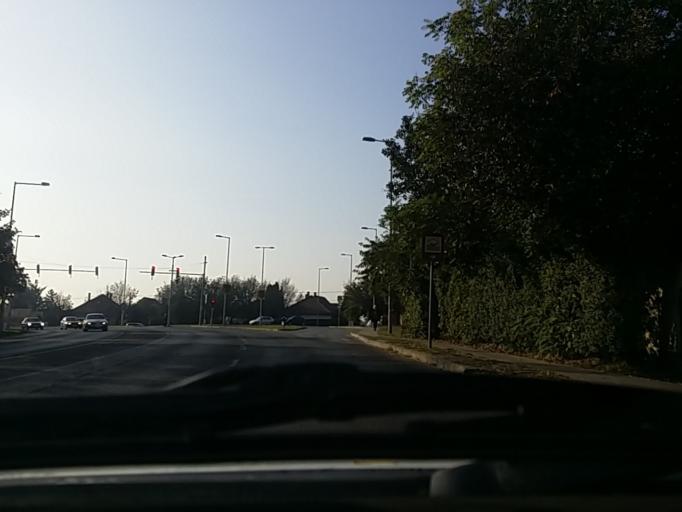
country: HU
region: Pest
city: Szentendre
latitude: 47.6653
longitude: 19.0713
